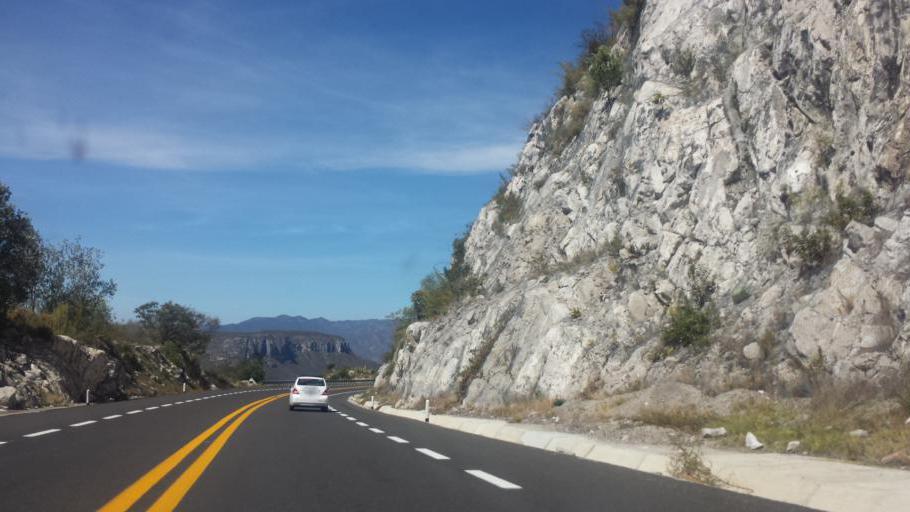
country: MX
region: Puebla
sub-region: San Jose Miahuatlan
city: San Pedro Tetitlan
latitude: 18.0286
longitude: -97.3481
